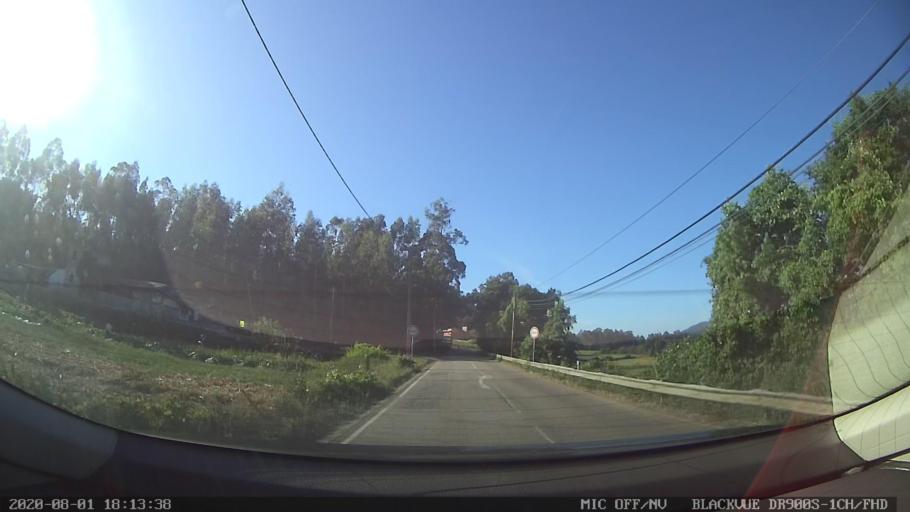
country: PT
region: Porto
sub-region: Pacos de Ferreira
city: Seroa
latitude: 41.2778
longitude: -8.4695
